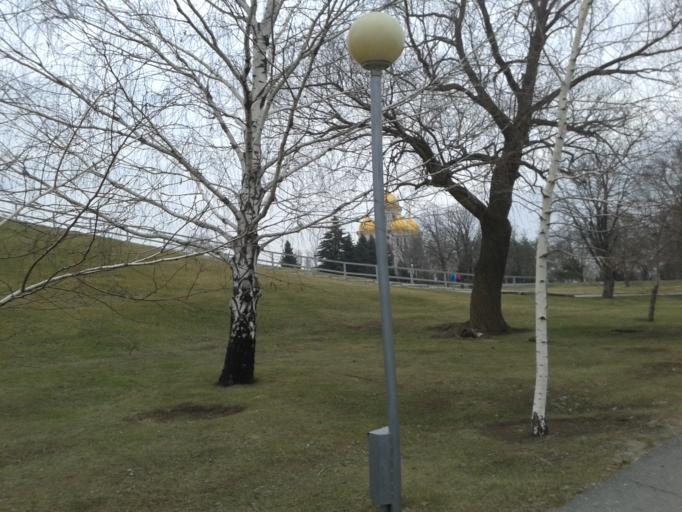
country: RU
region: Volgograd
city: Volgograd
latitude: 48.7425
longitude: 44.5362
